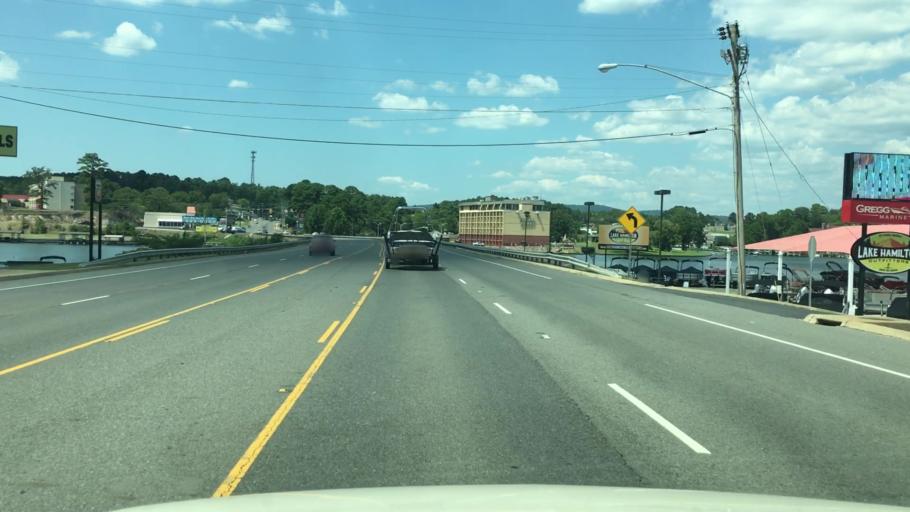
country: US
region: Arkansas
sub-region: Garland County
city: Lake Hamilton
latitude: 34.4395
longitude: -93.0884
